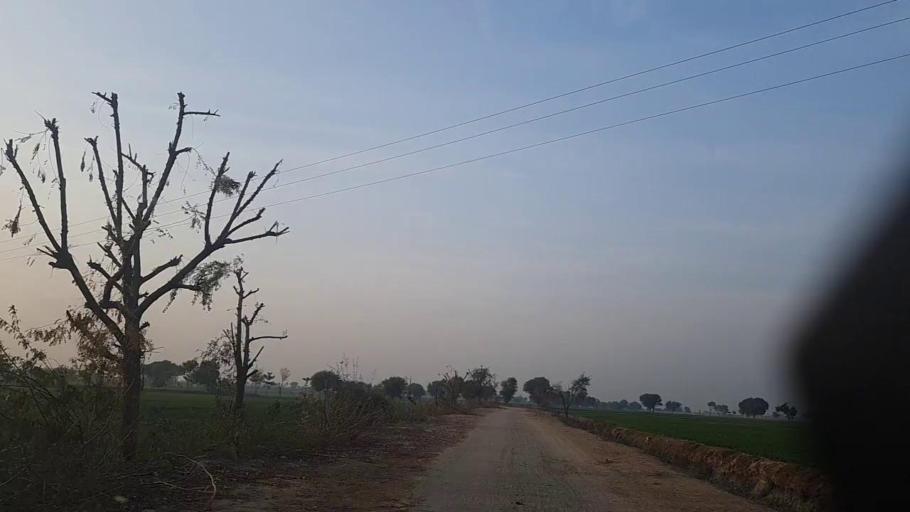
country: PK
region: Sindh
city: Sakrand
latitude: 26.1324
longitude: 68.2290
